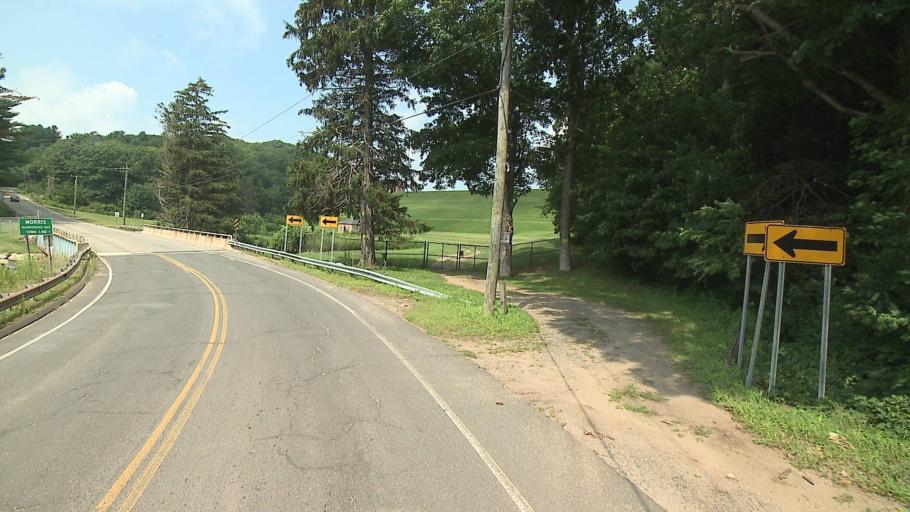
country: US
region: Connecticut
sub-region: Litchfield County
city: Thomaston
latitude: 41.6733
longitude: -73.1420
